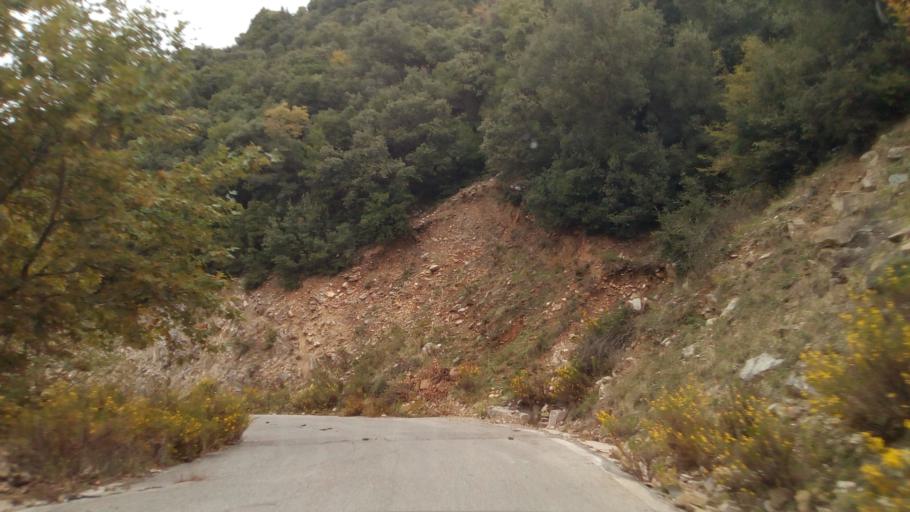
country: GR
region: West Greece
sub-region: Nomos Aitolias kai Akarnanias
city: Thermo
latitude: 38.6012
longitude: 21.8445
